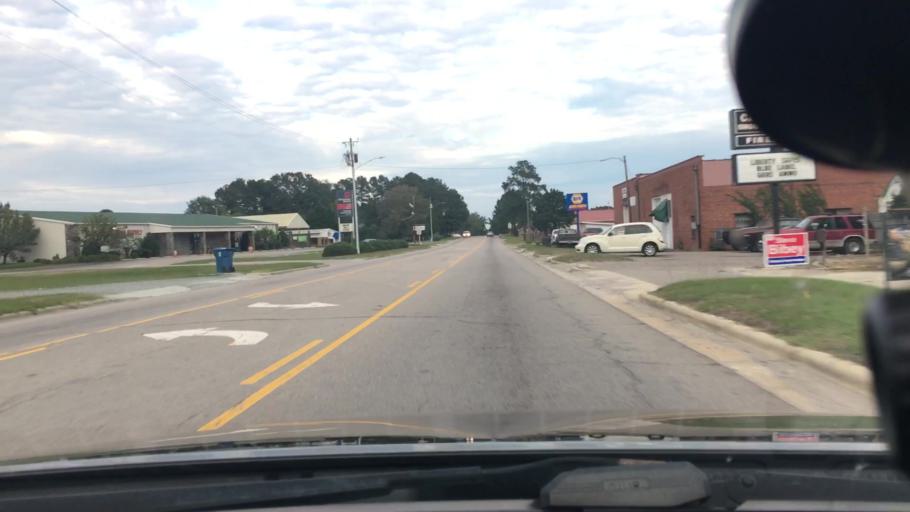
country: US
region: North Carolina
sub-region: Moore County
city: Carthage
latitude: 35.3438
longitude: -79.3927
